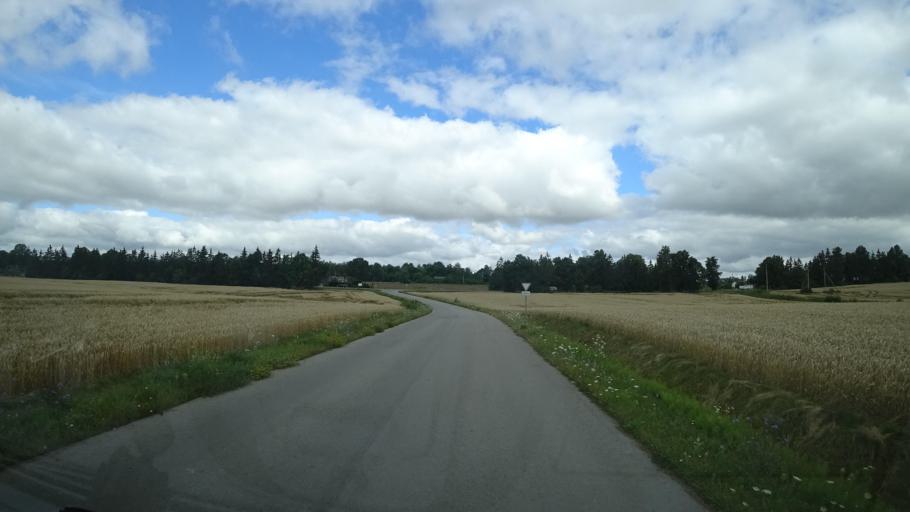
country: LT
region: Marijampoles apskritis
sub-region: Marijampole Municipality
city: Marijampole
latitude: 54.5197
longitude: 23.3206
